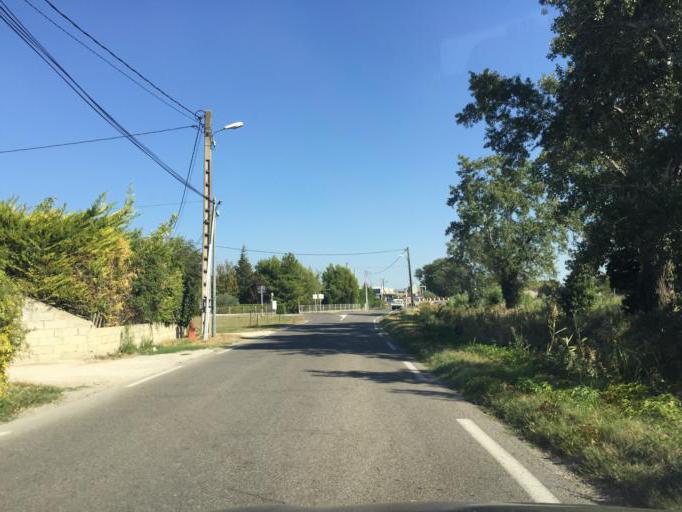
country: FR
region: Provence-Alpes-Cote d'Azur
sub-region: Departement du Vaucluse
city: Monteux
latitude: 44.0388
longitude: 4.9906
